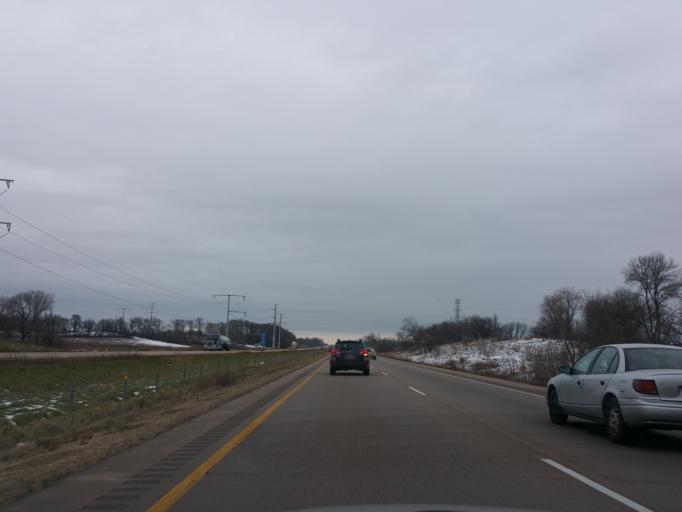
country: US
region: Wisconsin
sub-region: Dane County
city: Deerfield
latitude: 42.9884
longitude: -89.1333
